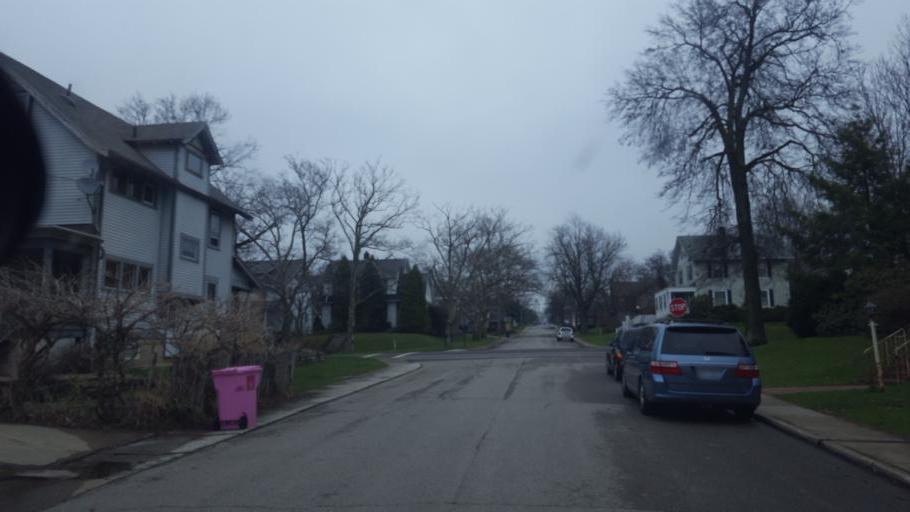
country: US
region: Ohio
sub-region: Richland County
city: Mansfield
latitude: 40.7576
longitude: -82.5398
